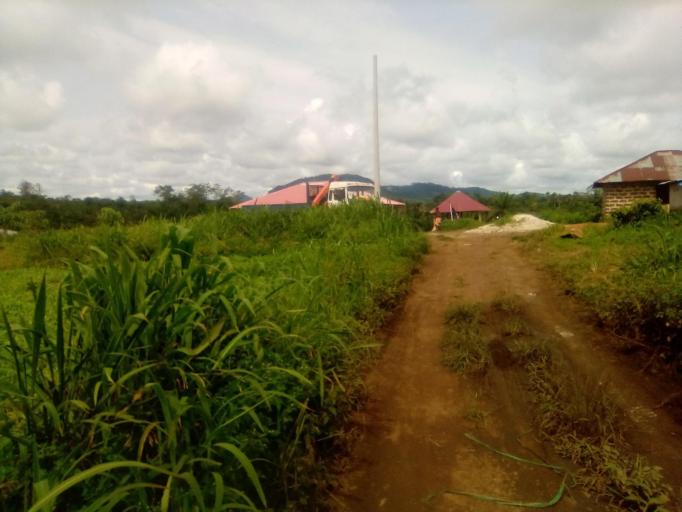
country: SL
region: Southern Province
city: Moyamba
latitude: 8.1449
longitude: -12.4312
